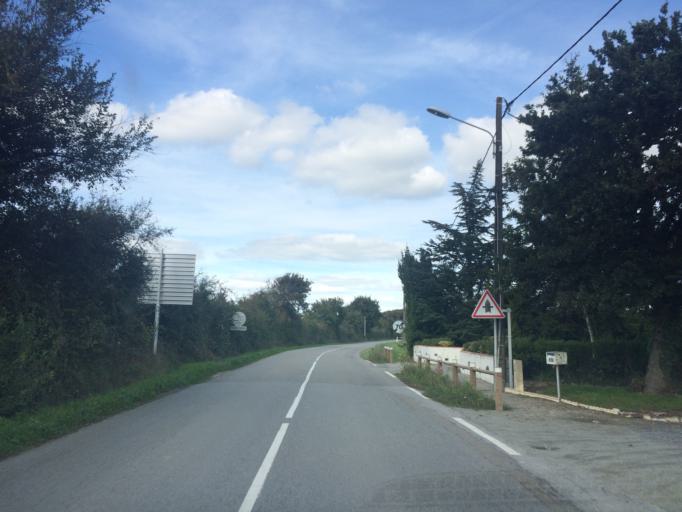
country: FR
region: Pays de la Loire
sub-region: Departement de la Loire-Atlantique
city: Chemere
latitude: 47.1303
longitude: -1.9105
